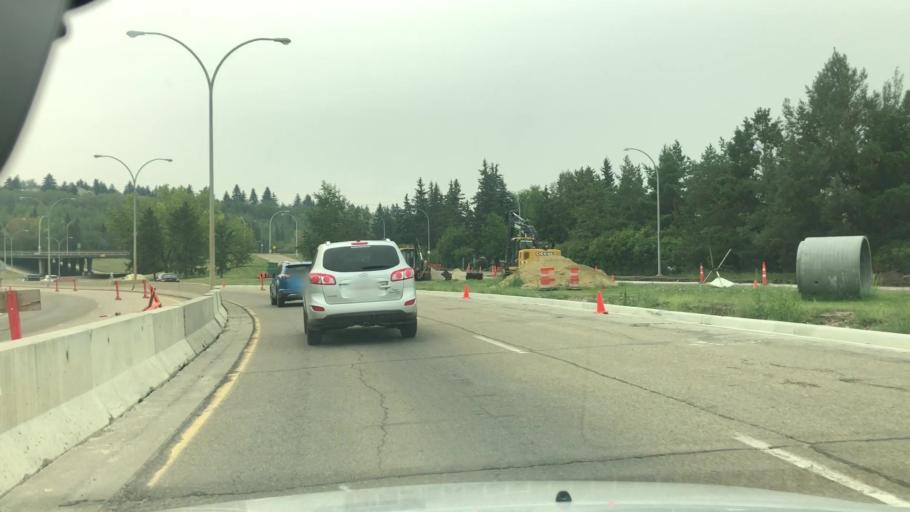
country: CA
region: Alberta
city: Edmonton
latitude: 53.5344
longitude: -113.5401
